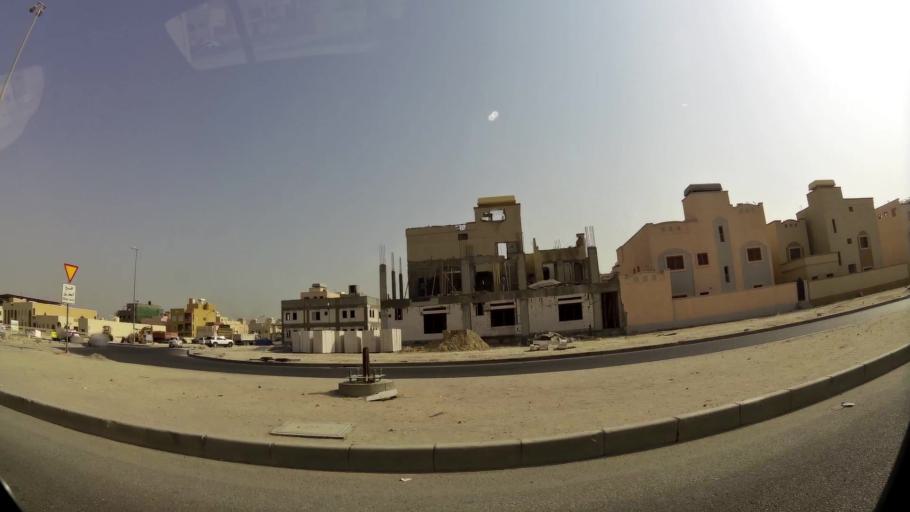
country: KW
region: Muhafazat al Jahra'
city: Al Jahra'
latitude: 29.3482
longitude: 47.7590
